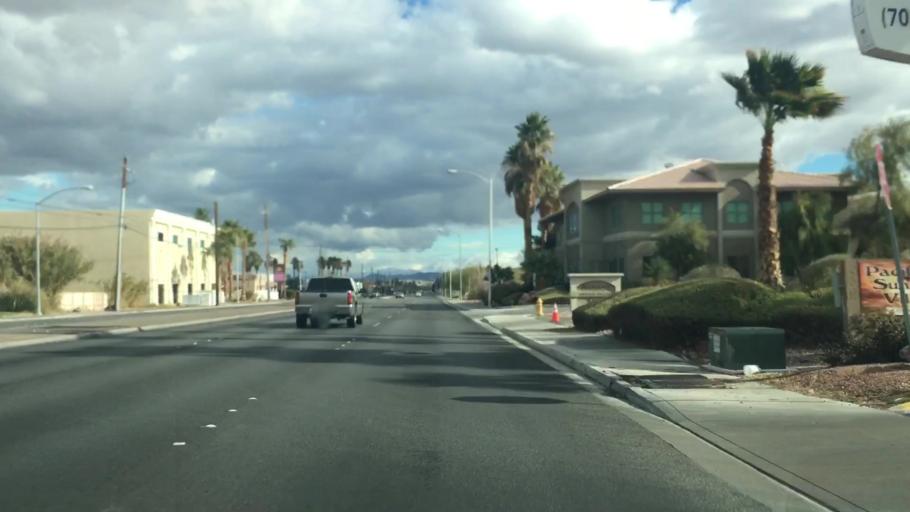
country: US
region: Nevada
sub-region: Clark County
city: Whitney
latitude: 36.0715
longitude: -115.1097
